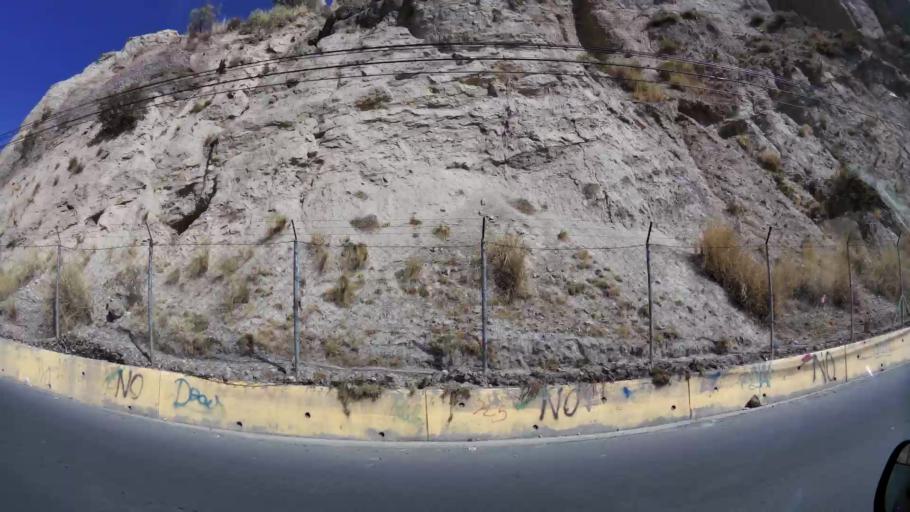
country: BO
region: La Paz
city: La Paz
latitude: -16.5246
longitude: -68.0931
